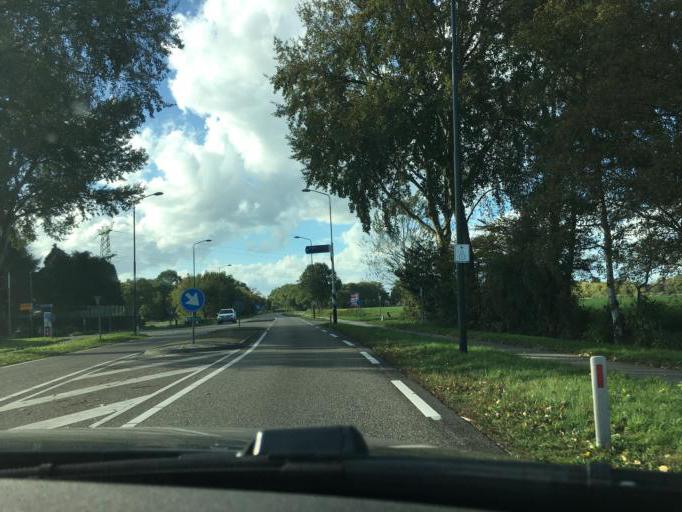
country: NL
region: North Brabant
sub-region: Gemeente Veghel
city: Eerde
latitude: 51.6072
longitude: 5.4933
